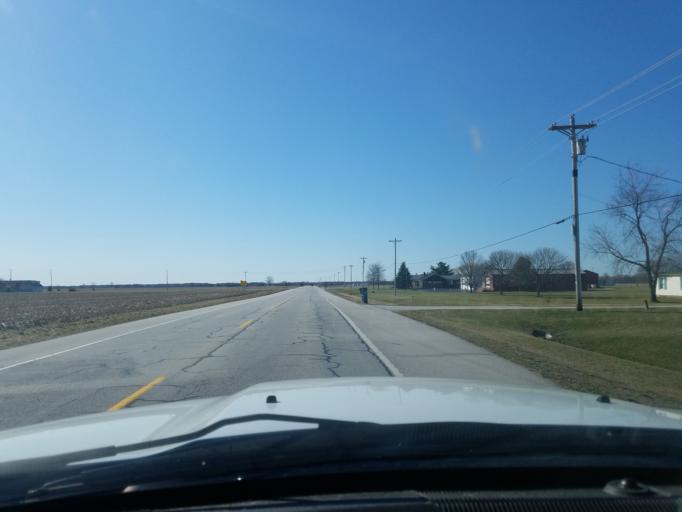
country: US
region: Indiana
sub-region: Shelby County
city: Shelbyville
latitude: 39.5044
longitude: -85.8195
